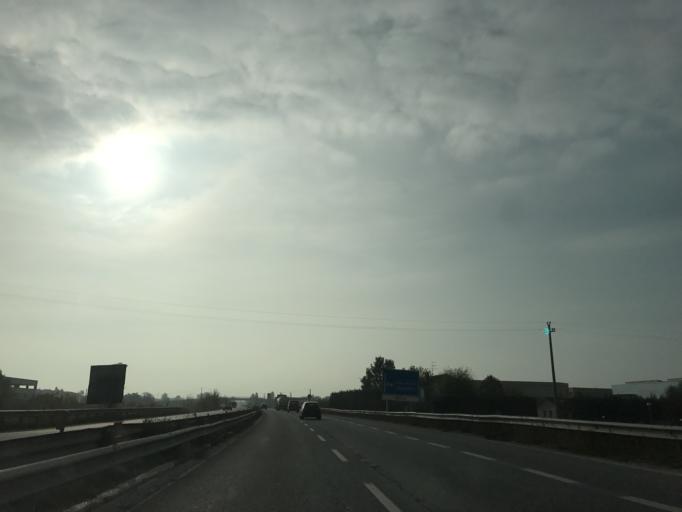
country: IT
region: Emilia-Romagna
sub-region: Forli-Cesena
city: Gatteo a Mare
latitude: 44.1779
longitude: 12.4140
